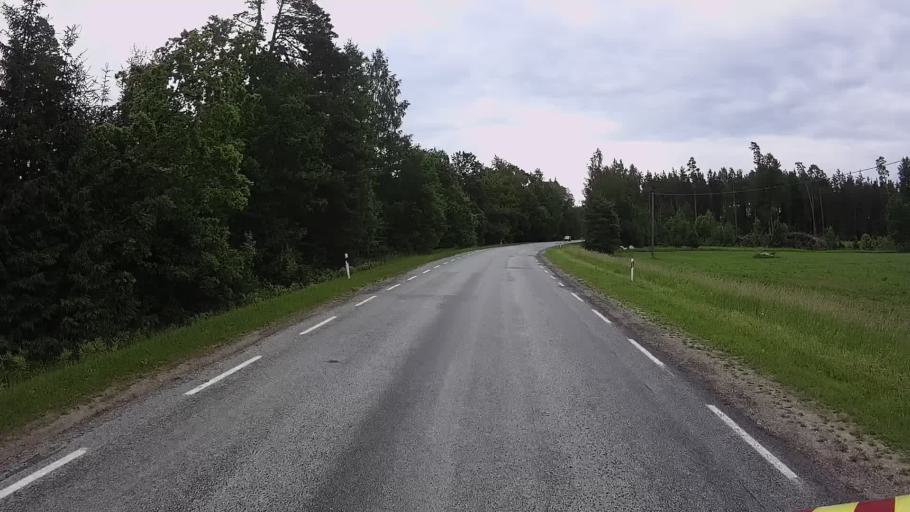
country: EE
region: Viljandimaa
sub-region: Karksi vald
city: Karksi-Nuia
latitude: 58.2246
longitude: 25.6126
